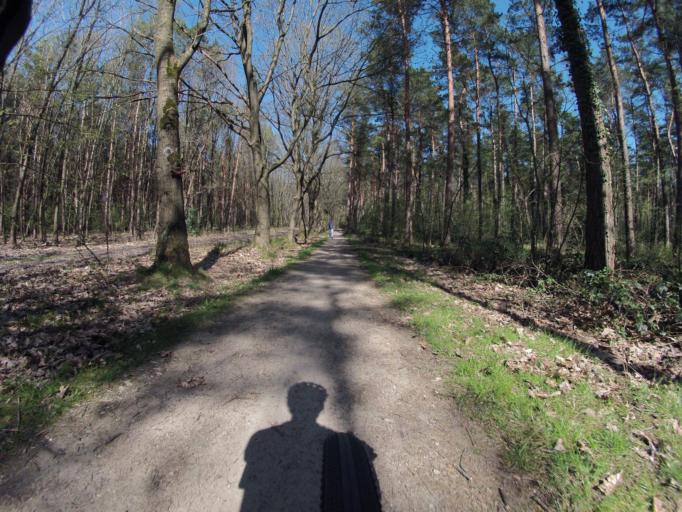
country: NL
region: Overijssel
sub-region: Gemeente Losser
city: Losser
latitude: 52.2785
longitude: 7.0510
